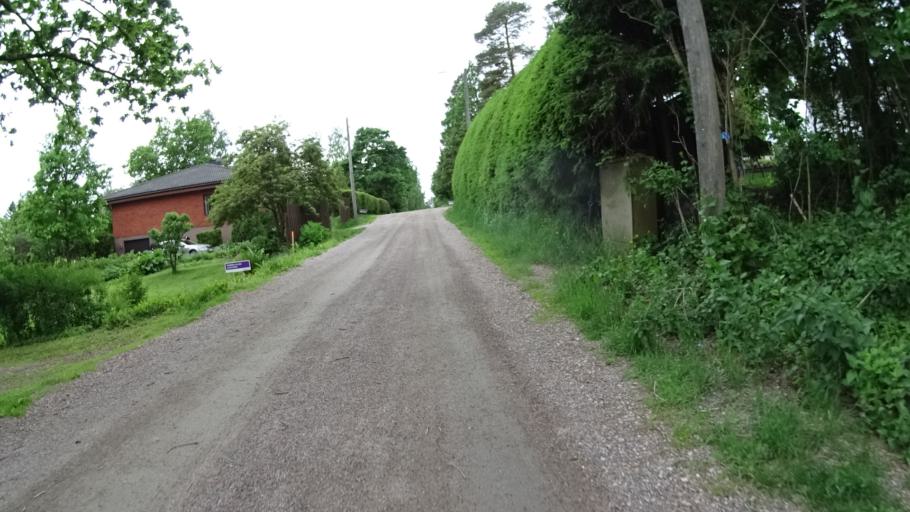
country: FI
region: Uusimaa
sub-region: Helsinki
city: Kilo
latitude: 60.2484
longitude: 24.7590
